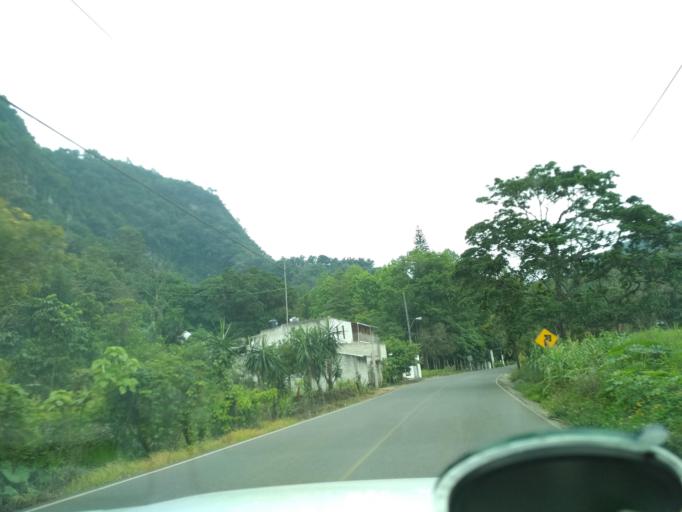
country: MX
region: Veracruz
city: Jilotepec
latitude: 19.6155
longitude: -96.9309
